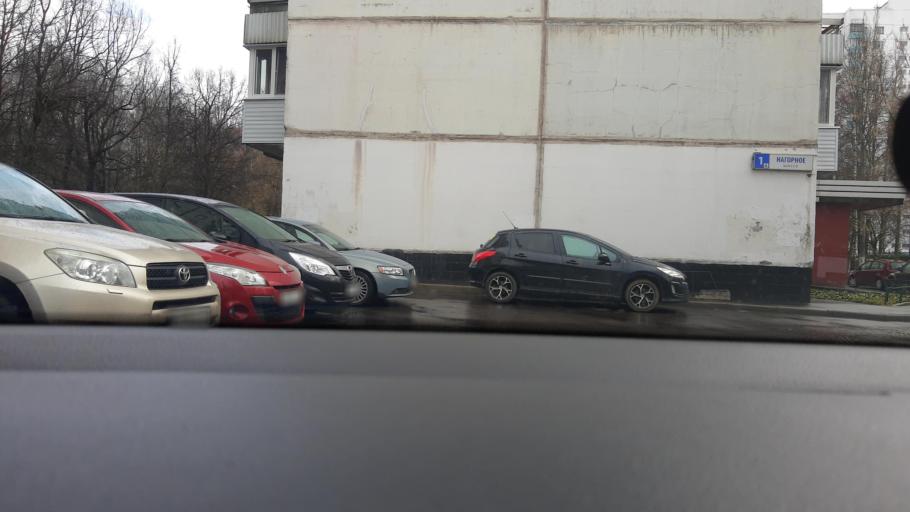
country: RU
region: Moscow
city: Khimki
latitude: 55.8940
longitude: 37.4137
